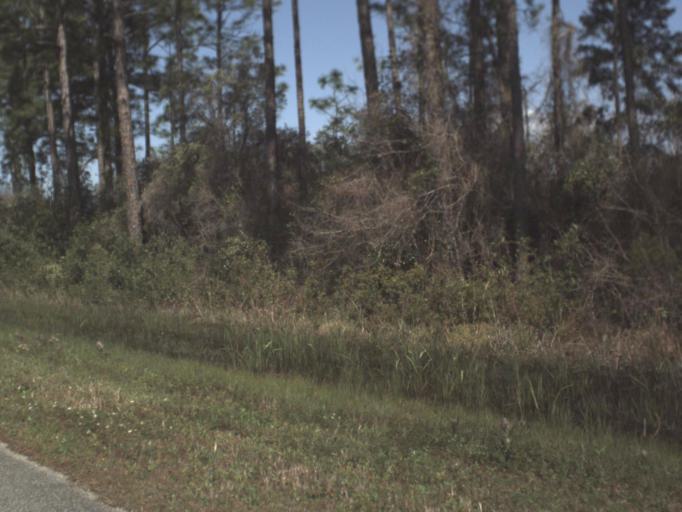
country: US
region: Florida
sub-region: Gulf County
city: Port Saint Joe
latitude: 29.7422
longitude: -85.2286
